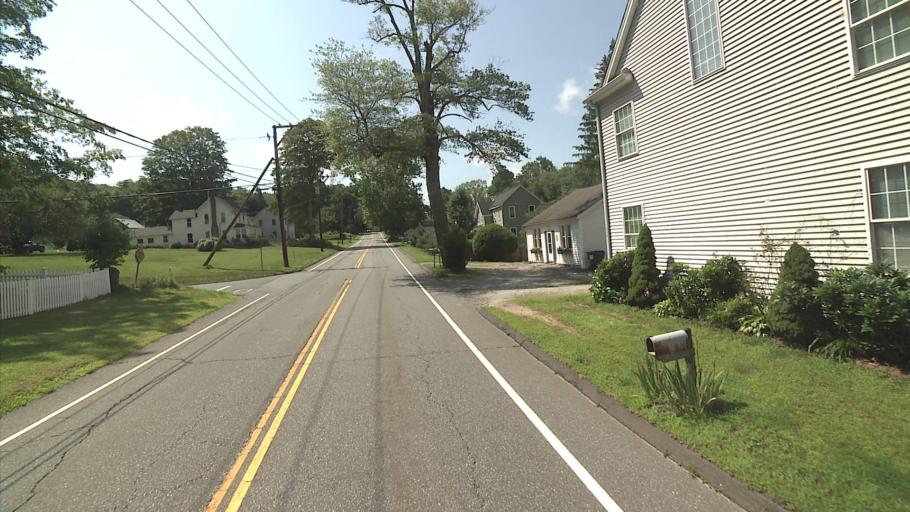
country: US
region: Connecticut
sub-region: Middlesex County
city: Deep River Center
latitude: 41.3596
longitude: -72.4470
